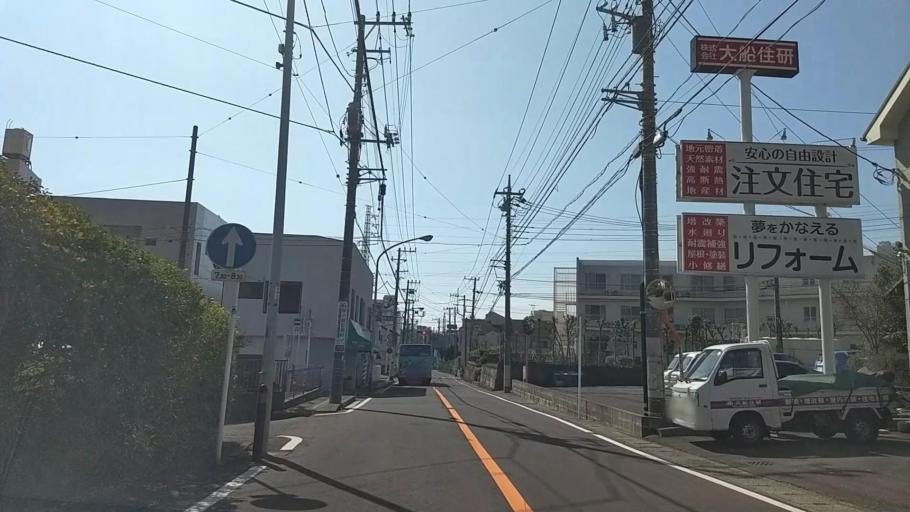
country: JP
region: Kanagawa
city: Kamakura
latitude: 35.3652
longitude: 139.5404
